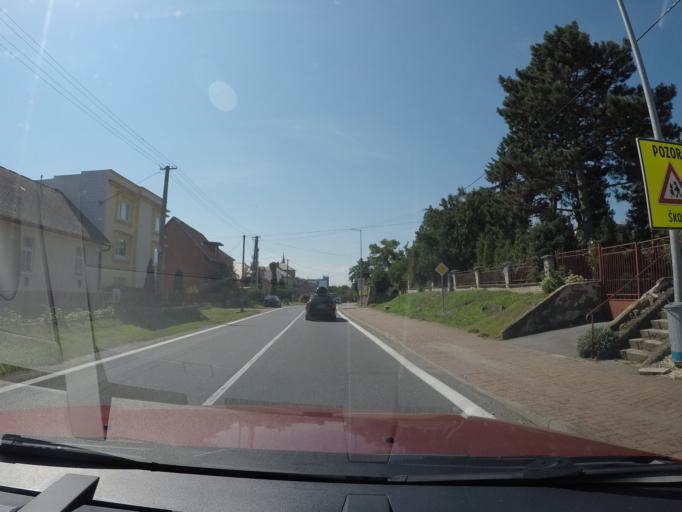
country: SK
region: Presovsky
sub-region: Okres Presov
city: Presov
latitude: 48.9268
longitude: 21.2413
